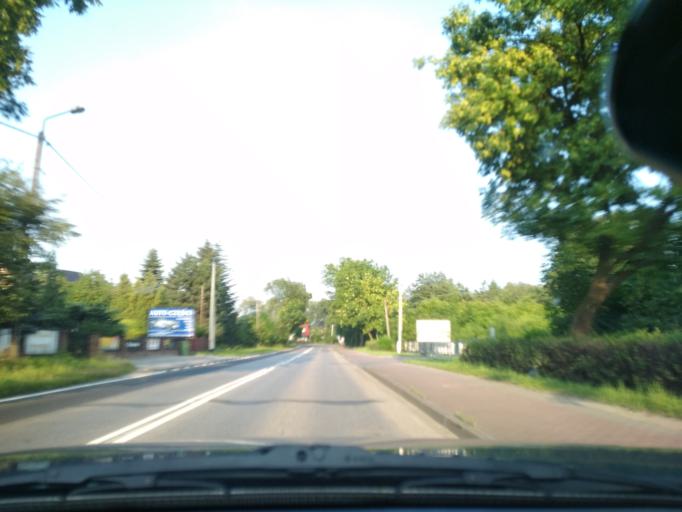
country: PL
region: Silesian Voivodeship
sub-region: Powiat zawiercianski
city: Ogrodzieniec
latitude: 50.4542
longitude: 19.5084
